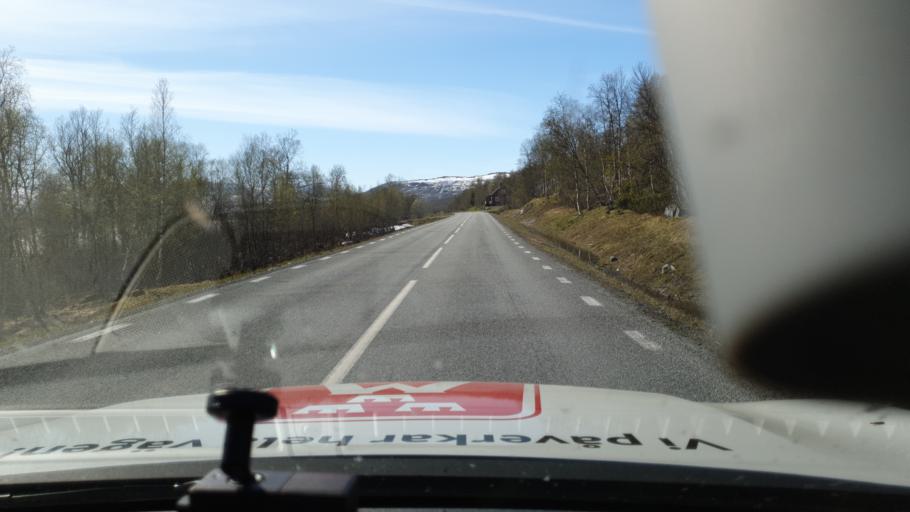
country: NO
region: Nordland
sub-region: Rana
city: Mo i Rana
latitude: 66.0422
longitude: 14.9915
